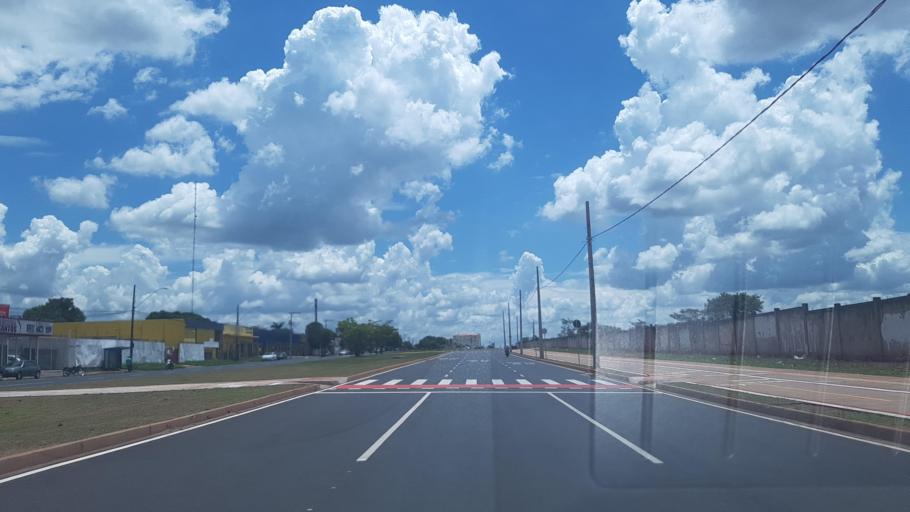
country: BR
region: Minas Gerais
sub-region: Uberlandia
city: Uberlandia
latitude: -18.9556
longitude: -48.3310
